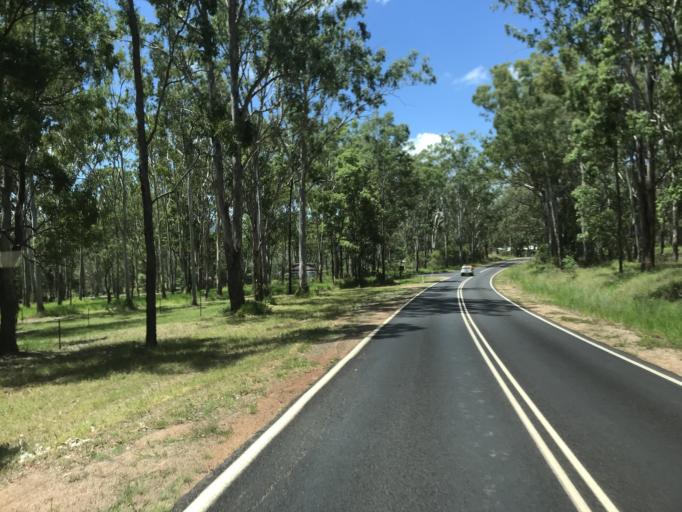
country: AU
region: Queensland
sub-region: Tablelands
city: Atherton
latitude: -17.4185
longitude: 145.3929
